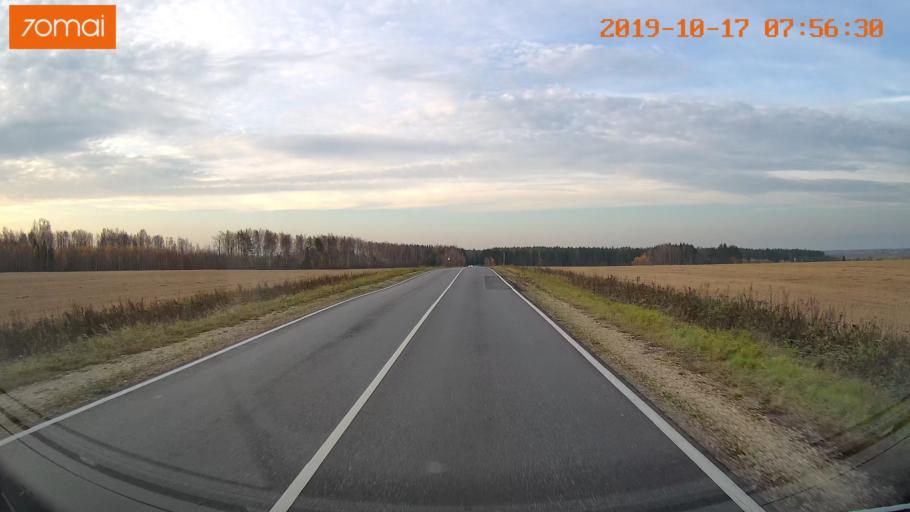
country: RU
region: Vladimir
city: Bavleny
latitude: 56.4223
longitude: 39.5897
